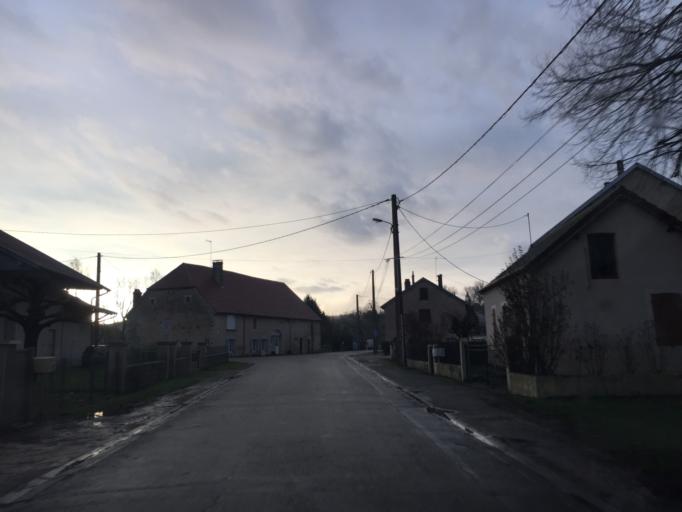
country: FR
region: Franche-Comte
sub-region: Departement du Jura
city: Choisey
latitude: 47.0191
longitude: 5.4881
